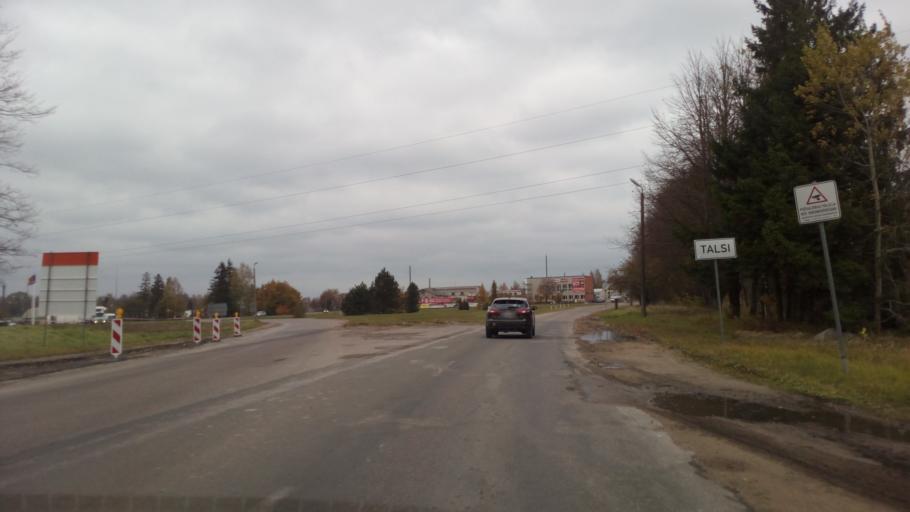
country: LV
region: Talsu Rajons
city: Talsi
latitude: 57.2314
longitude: 22.5856
